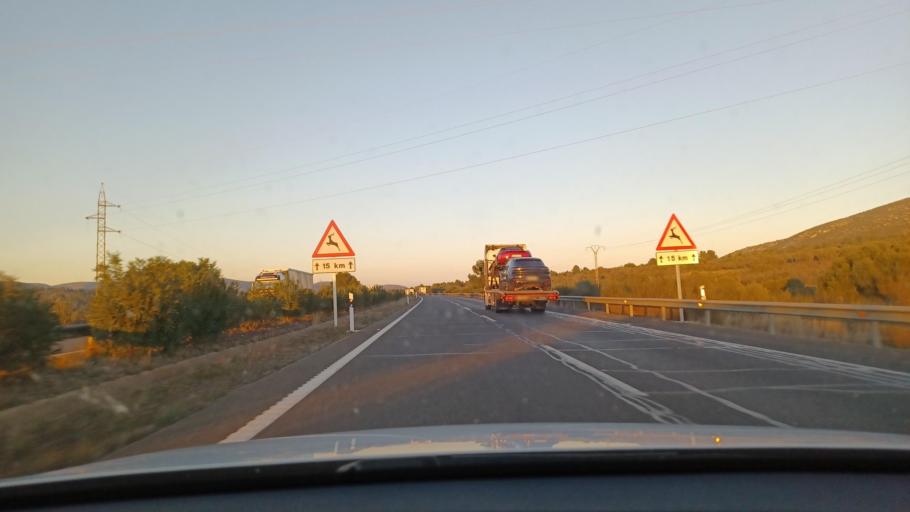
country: ES
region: Valencia
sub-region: Provincia de Castello
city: Alcala de Xivert
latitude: 40.3326
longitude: 0.2634
